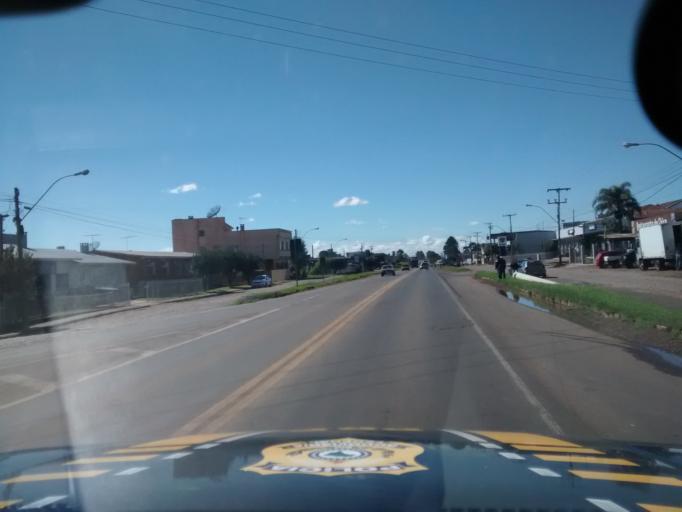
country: BR
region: Rio Grande do Sul
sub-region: Vacaria
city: Vacaria
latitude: -28.5090
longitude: -50.9290
